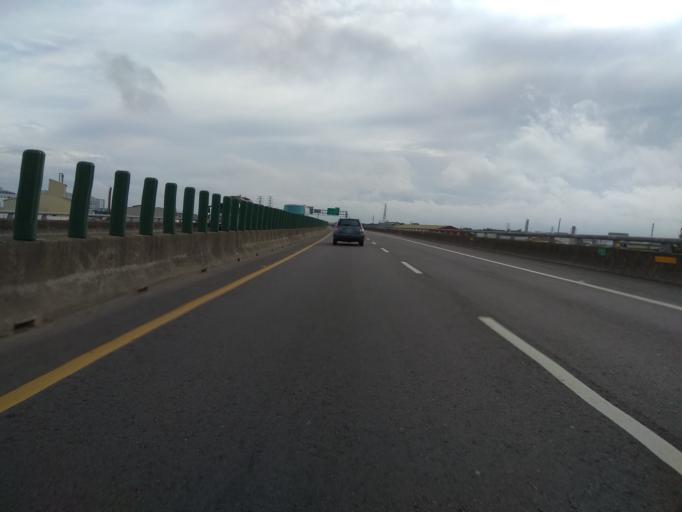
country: TW
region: Taiwan
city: Daxi
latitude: 24.8995
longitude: 121.2429
